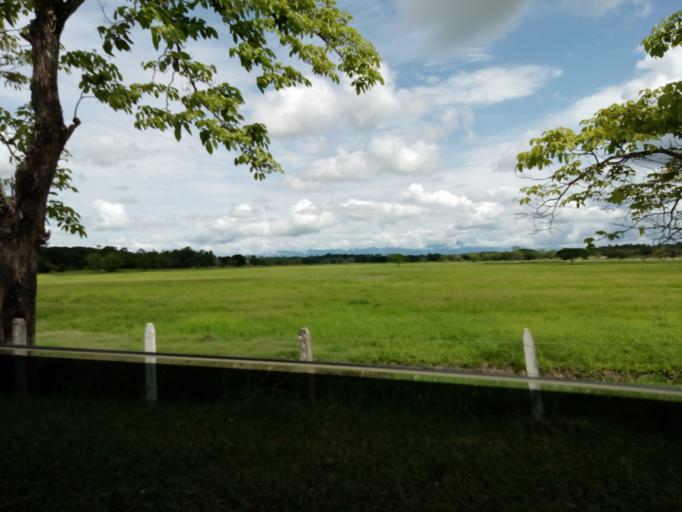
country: CO
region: Boyaca
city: Puerto Boyaca
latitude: 5.9431
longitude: -74.5697
